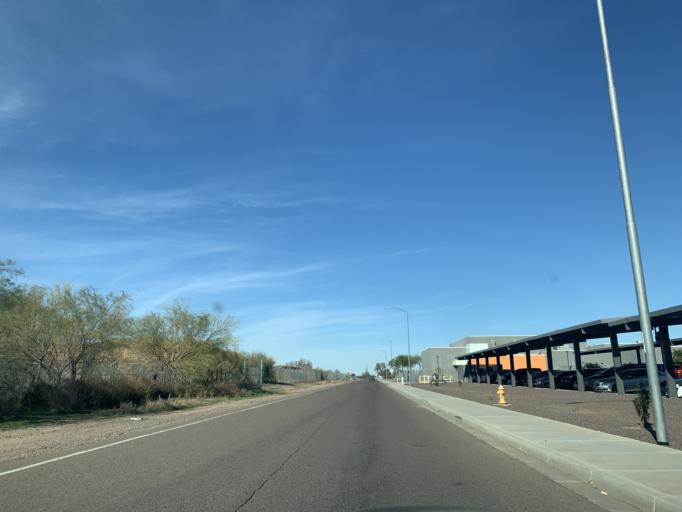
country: US
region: Arizona
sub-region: Maricopa County
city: Laveen
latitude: 33.3989
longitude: -112.1422
